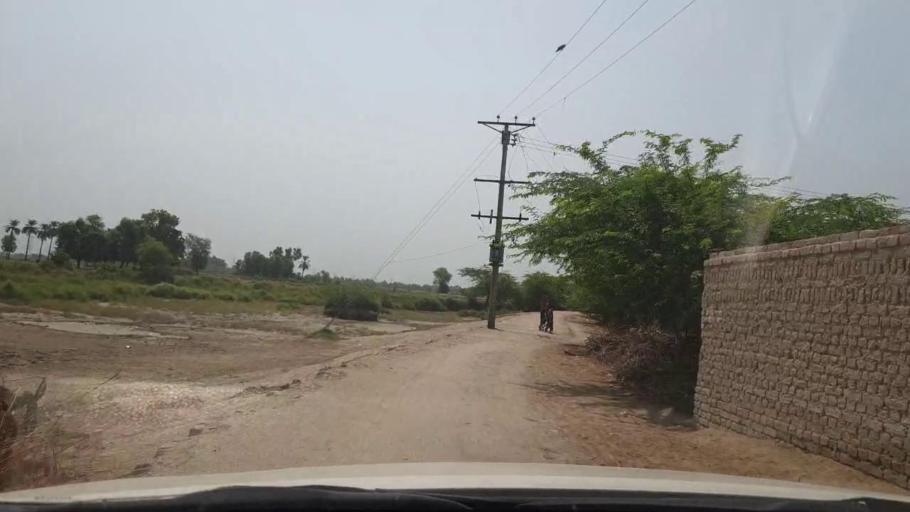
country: PK
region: Sindh
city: Shikarpur
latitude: 27.9872
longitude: 68.7164
